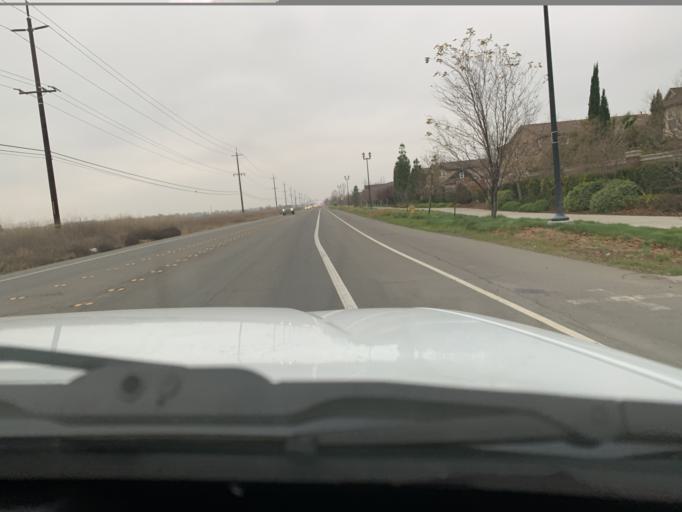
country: US
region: California
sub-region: Yolo County
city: Woodland
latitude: 38.6532
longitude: -121.7289
